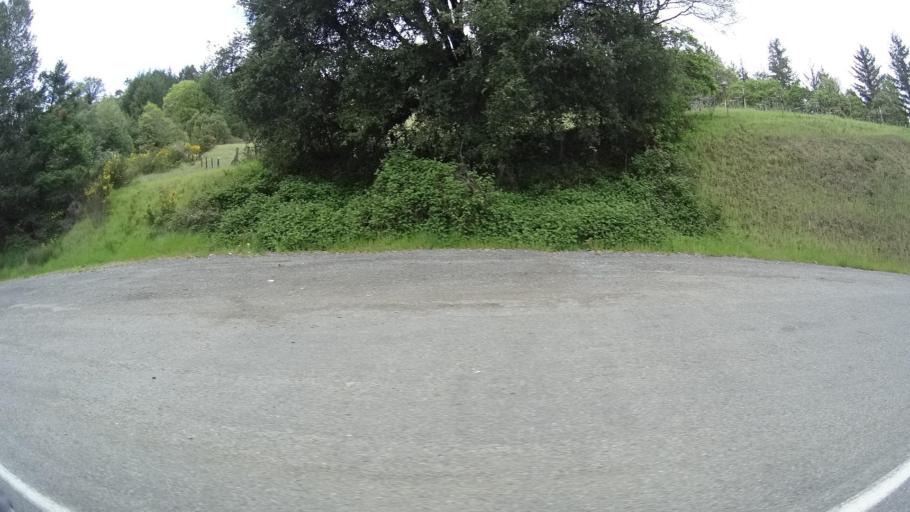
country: US
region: California
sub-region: Humboldt County
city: Redway
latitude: 40.1111
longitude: -123.8970
